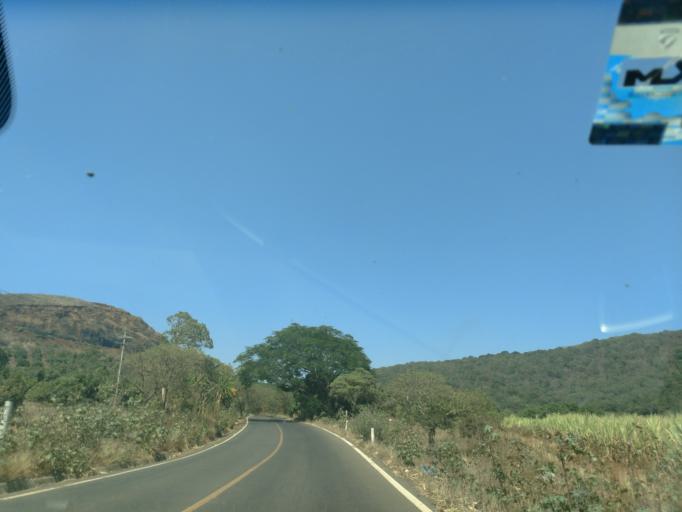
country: MX
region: Nayarit
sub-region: Tepic
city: La Corregidora
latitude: 21.4990
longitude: -104.7775
